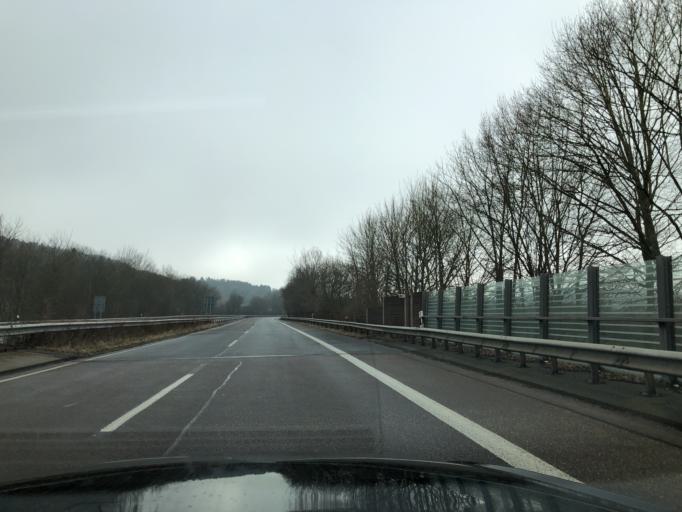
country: DE
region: Rheinland-Pfalz
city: Konigsfeld
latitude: 50.5434
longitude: 7.1968
